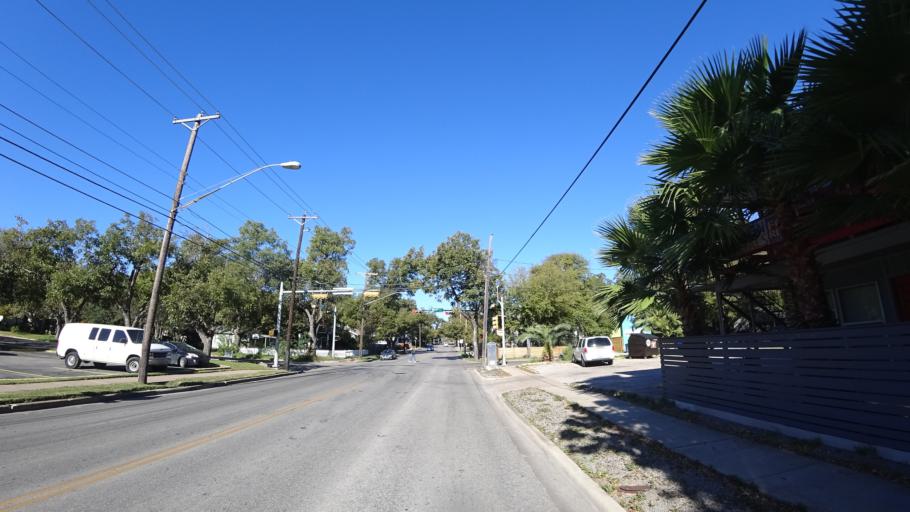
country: US
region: Texas
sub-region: Travis County
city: Austin
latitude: 30.3085
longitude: -97.7280
